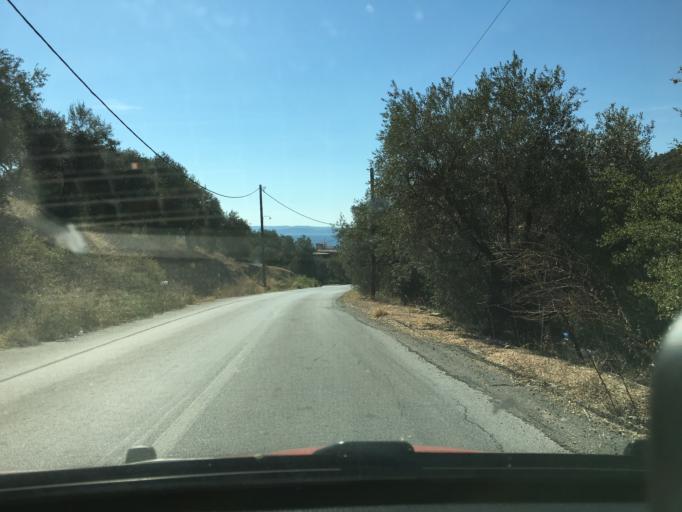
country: GR
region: Central Macedonia
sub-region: Nomos Chalkidikis
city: Agios Nikolaos
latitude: 40.3386
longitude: 23.7201
